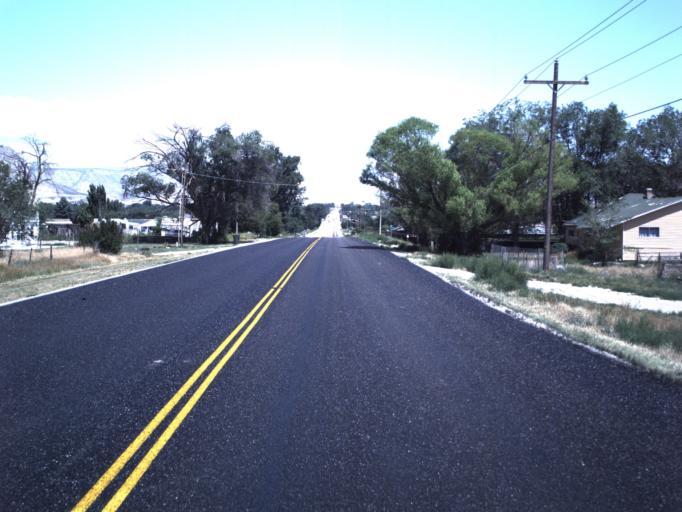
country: US
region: Utah
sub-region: Emery County
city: Ferron
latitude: 39.0766
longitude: -111.1317
